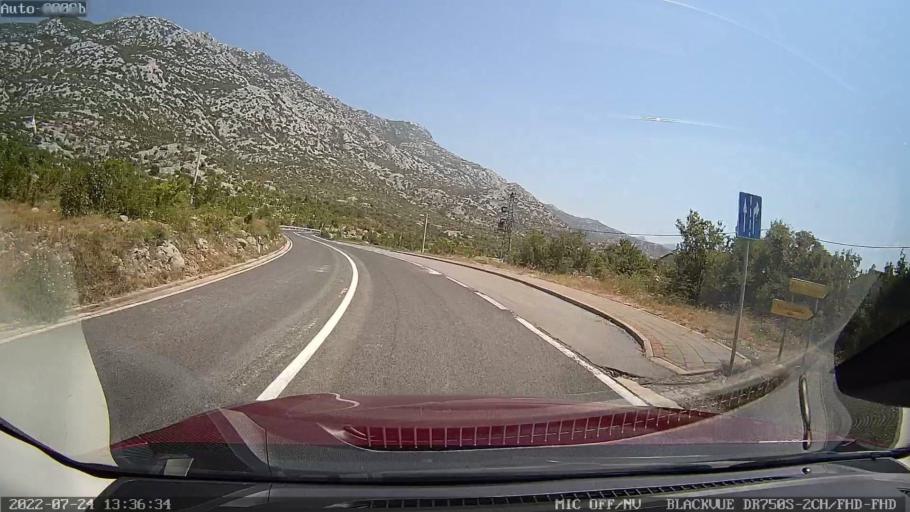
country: HR
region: Licko-Senjska
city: Karlobag
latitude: 44.5625
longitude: 15.0244
